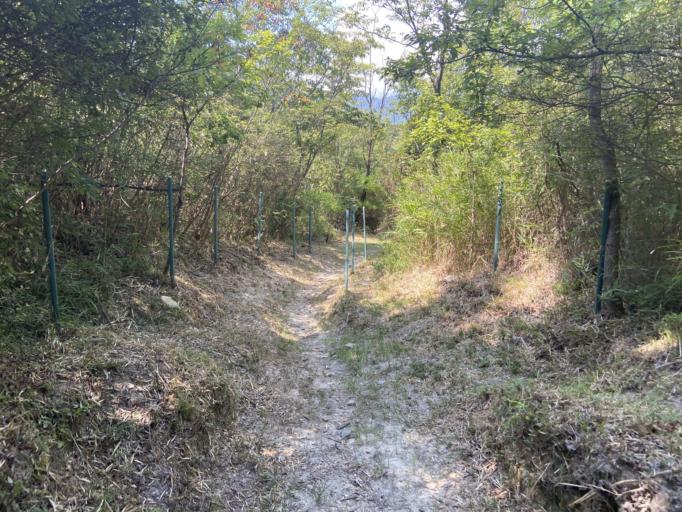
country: JP
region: Hyogo
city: Takarazuka
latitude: 34.7785
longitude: 135.3390
